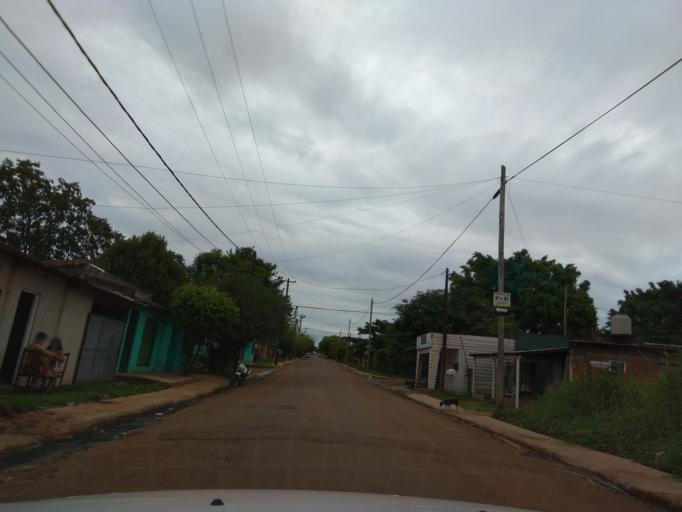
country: AR
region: Misiones
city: Garupa
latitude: -27.4411
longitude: -55.8645
